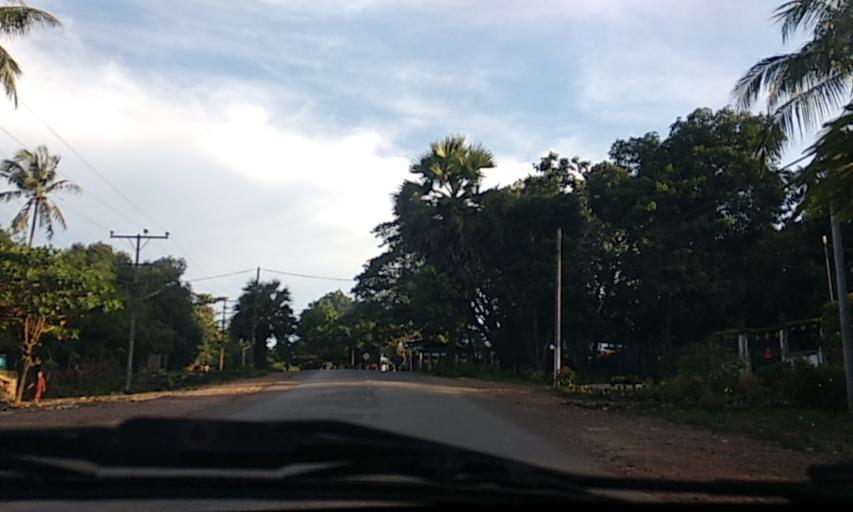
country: MM
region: Mon
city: Mawlamyine
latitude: 16.4024
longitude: 97.7019
